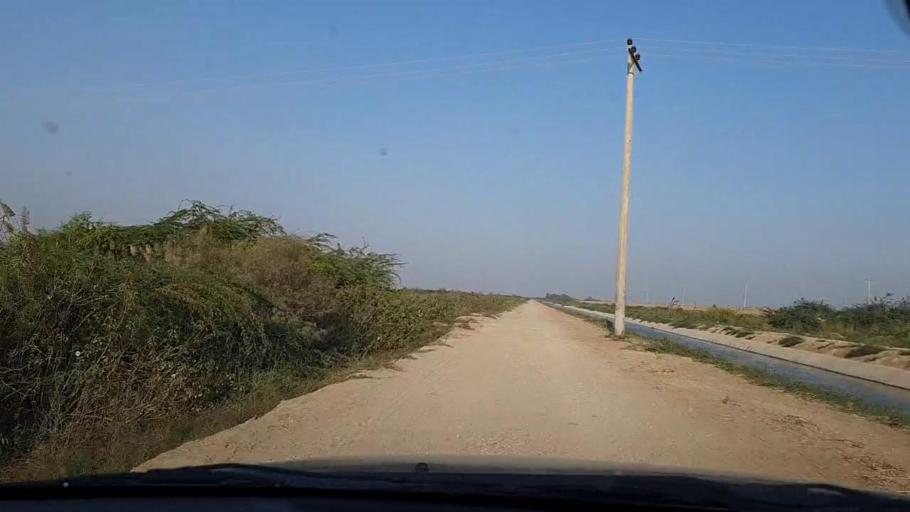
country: PK
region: Sindh
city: Chuhar Jamali
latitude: 24.2812
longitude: 67.7430
